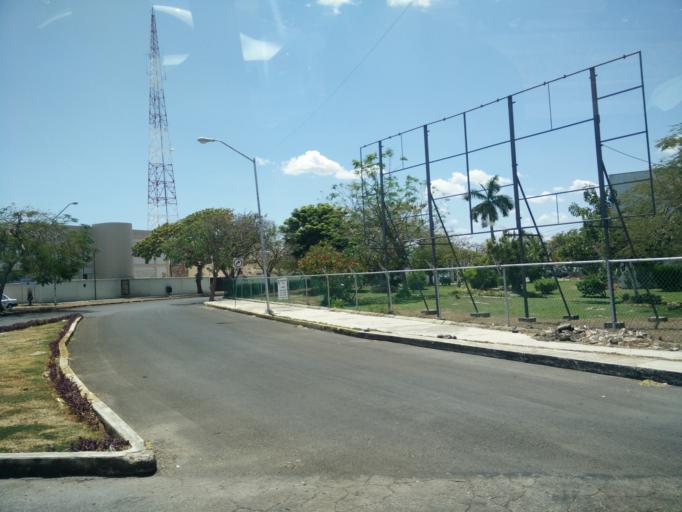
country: MX
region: Yucatan
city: Merida
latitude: 21.0267
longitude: -89.6248
